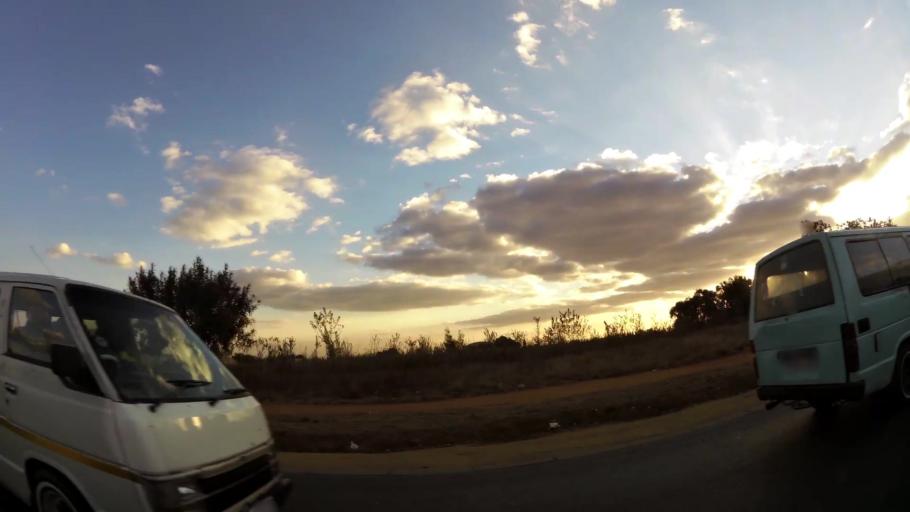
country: ZA
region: Gauteng
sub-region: City of Johannesburg Metropolitan Municipality
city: Midrand
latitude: -25.9919
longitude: 28.1539
